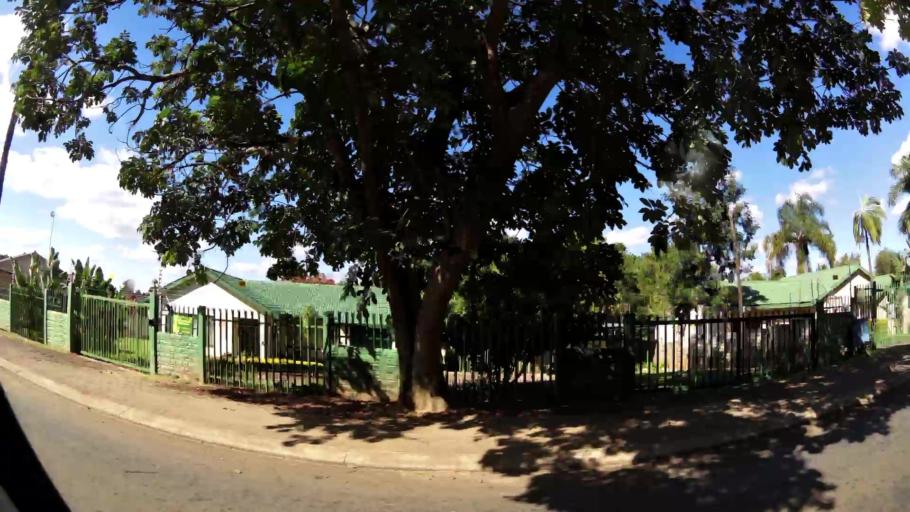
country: ZA
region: Limpopo
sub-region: Mopani District Municipality
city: Tzaneen
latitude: -23.8200
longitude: 30.1491
